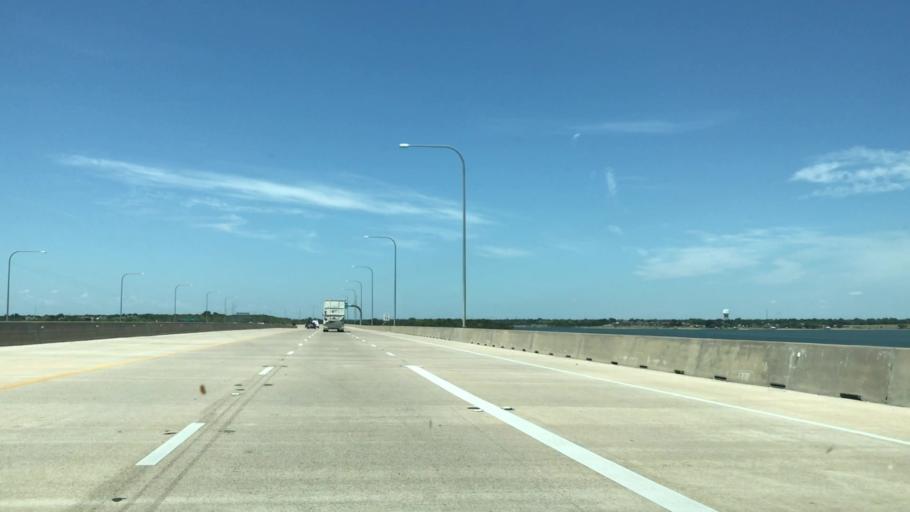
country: US
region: Texas
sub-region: Dallas County
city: Rowlett
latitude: 32.8665
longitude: -96.5536
